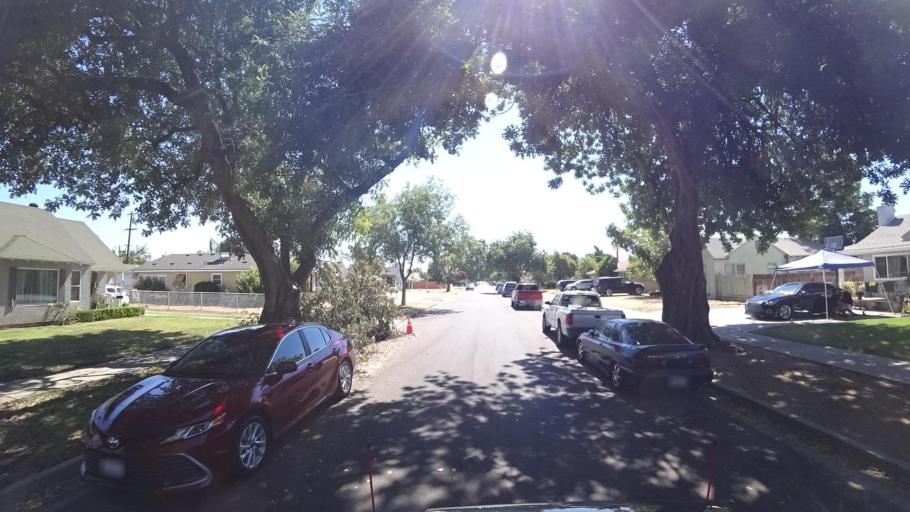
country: US
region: California
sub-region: Fresno County
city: Fresno
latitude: 36.7459
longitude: -119.7378
